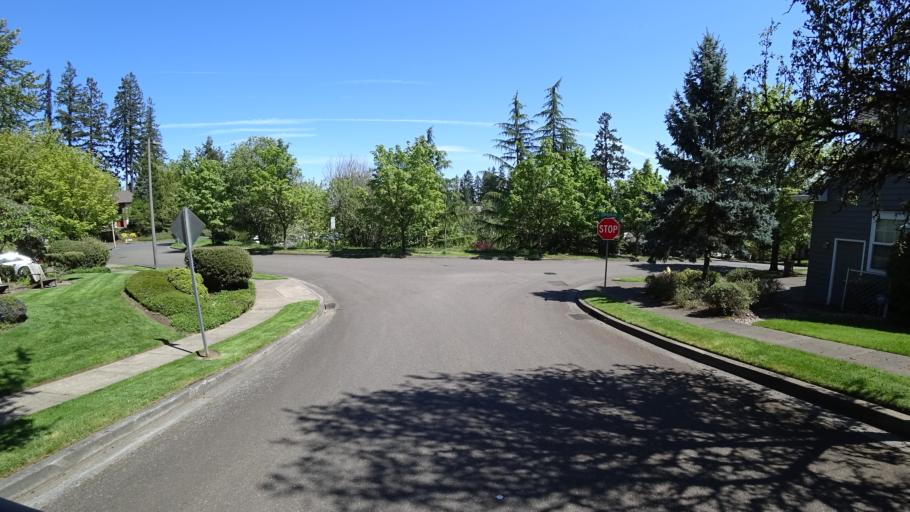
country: US
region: Oregon
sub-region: Washington County
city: Aloha
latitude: 45.4455
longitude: -122.8455
